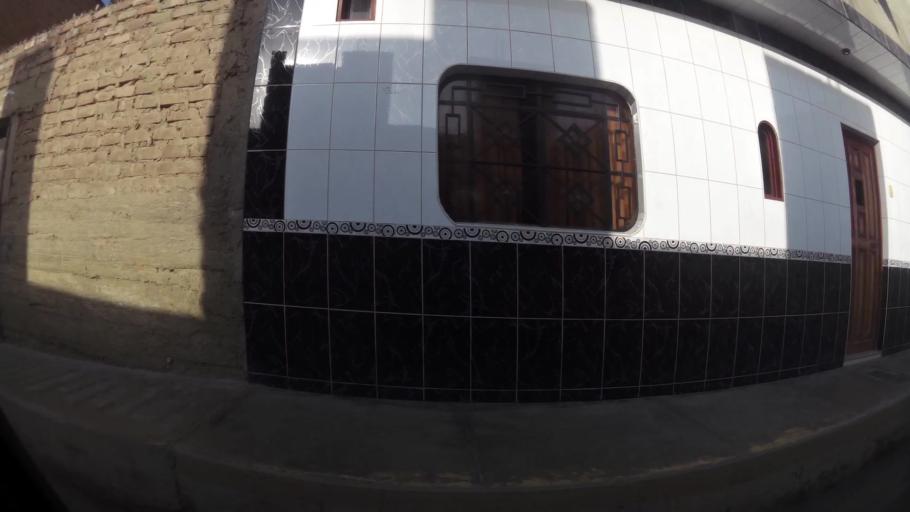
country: PE
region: Lima
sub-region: Huaura
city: Huacho
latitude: -11.1113
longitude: -77.6040
